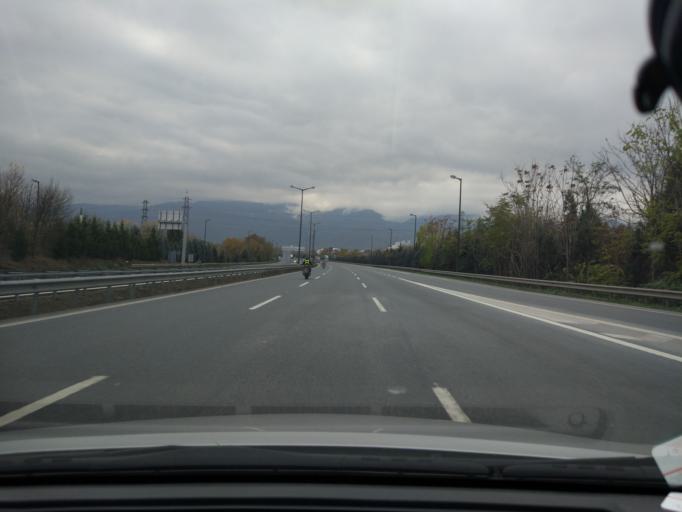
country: TR
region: Kocaeli
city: Kosekoy
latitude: 40.7460
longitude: 30.0417
